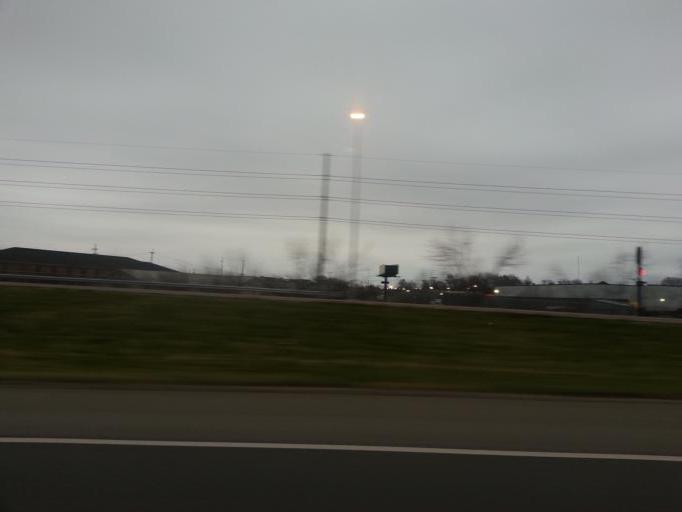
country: US
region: Iowa
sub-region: Linn County
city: Hiawatha
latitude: 42.0254
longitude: -91.6709
